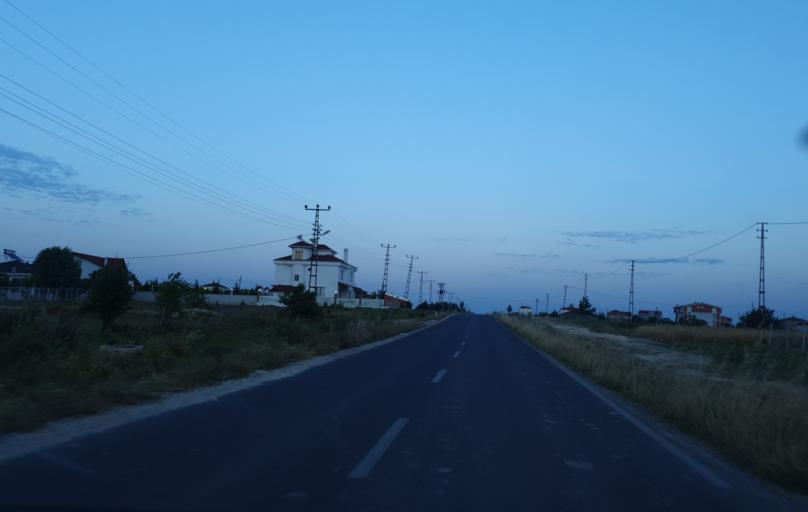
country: TR
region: Tekirdag
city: Velimese
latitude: 41.3445
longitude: 27.8956
